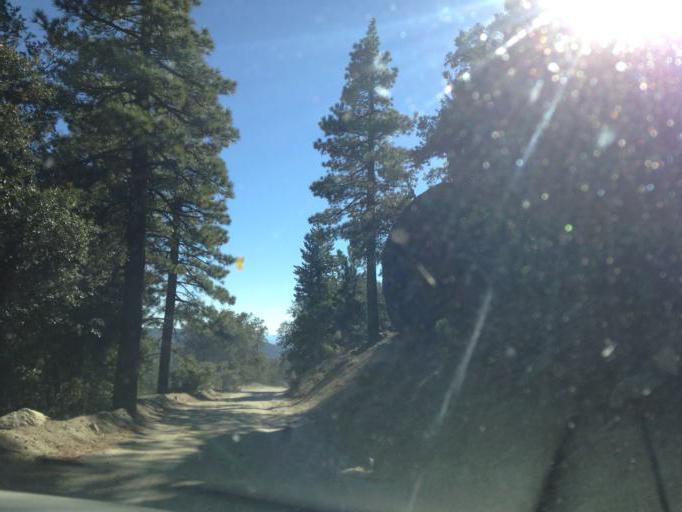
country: US
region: California
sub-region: Riverside County
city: Idyllwild-Pine Cove
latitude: 33.8150
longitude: -116.7495
